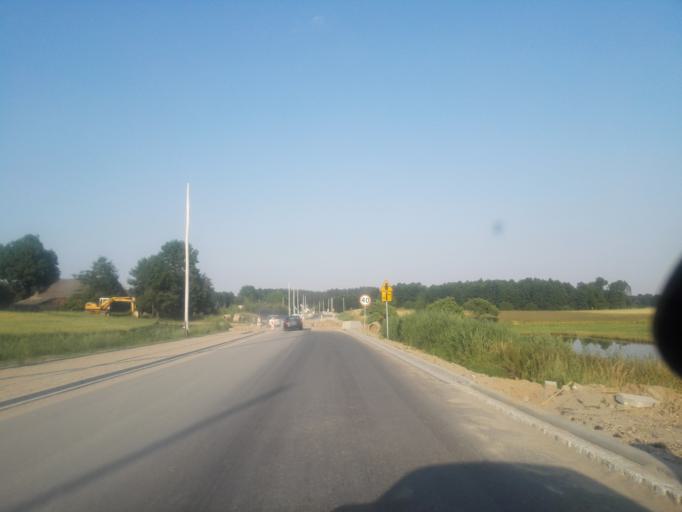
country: PL
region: Podlasie
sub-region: Powiat sejnenski
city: Krasnopol
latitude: 54.0826
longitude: 23.0839
